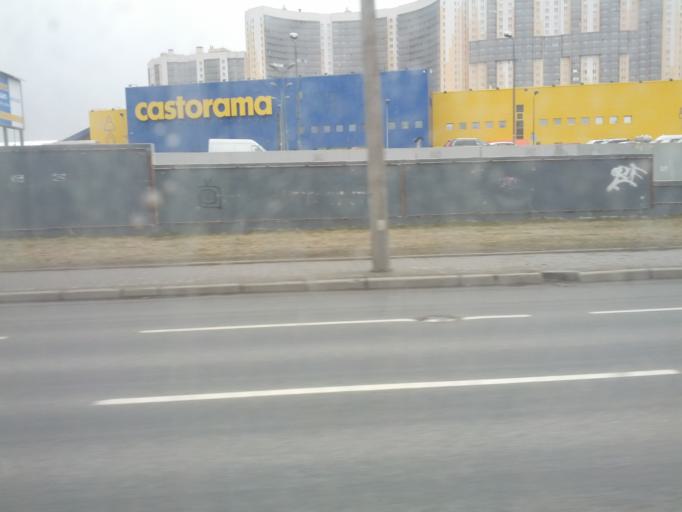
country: RU
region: St.-Petersburg
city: Obukhovo
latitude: 59.9077
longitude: 30.4490
